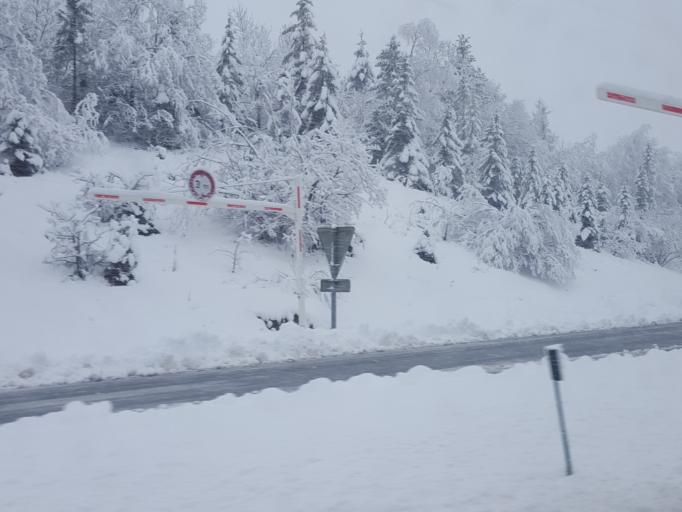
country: FR
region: Rhone-Alpes
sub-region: Departement de la Haute-Savoie
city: Evires
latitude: 46.0465
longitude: 6.2630
